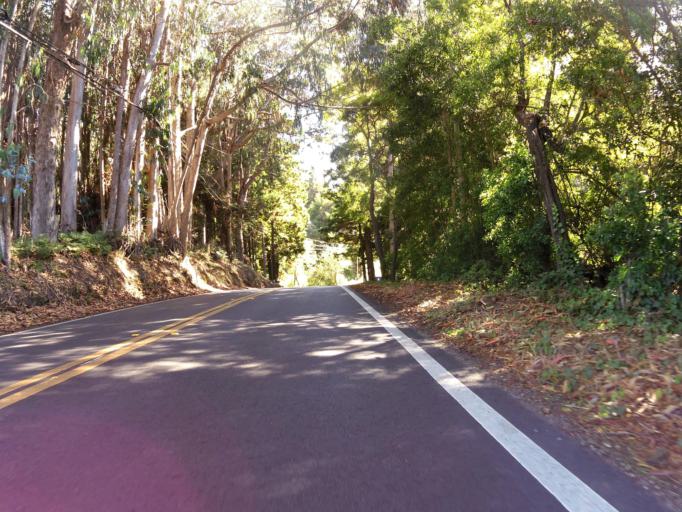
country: US
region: California
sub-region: Mendocino County
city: Fort Bragg
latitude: 39.5234
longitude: -123.7611
